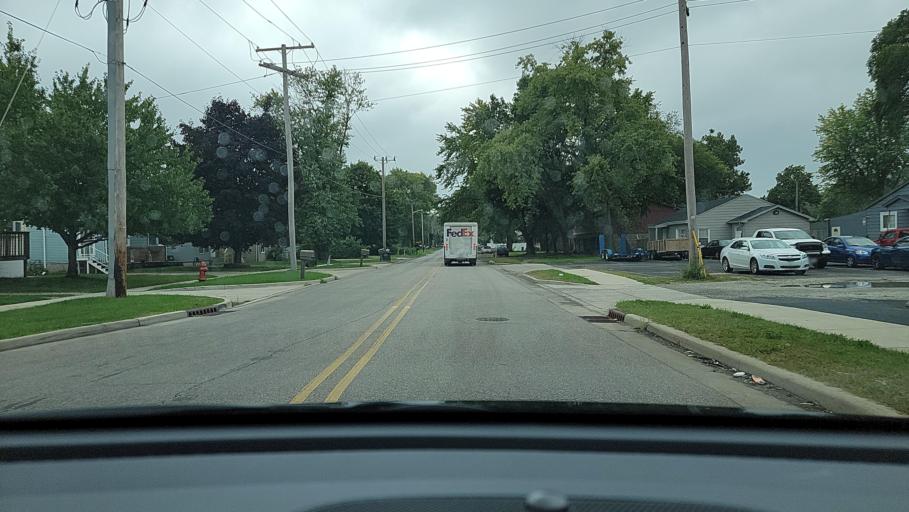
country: US
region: Indiana
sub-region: Lake County
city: Lake Station
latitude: 41.5741
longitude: -87.2220
